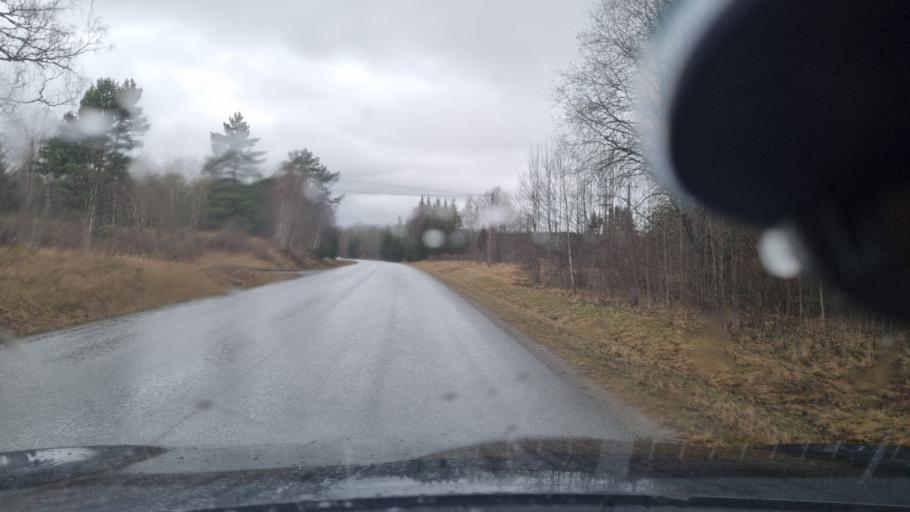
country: SE
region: Stockholm
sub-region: Upplands-Bro Kommun
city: Kungsaengen
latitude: 59.5324
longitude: 17.7487
